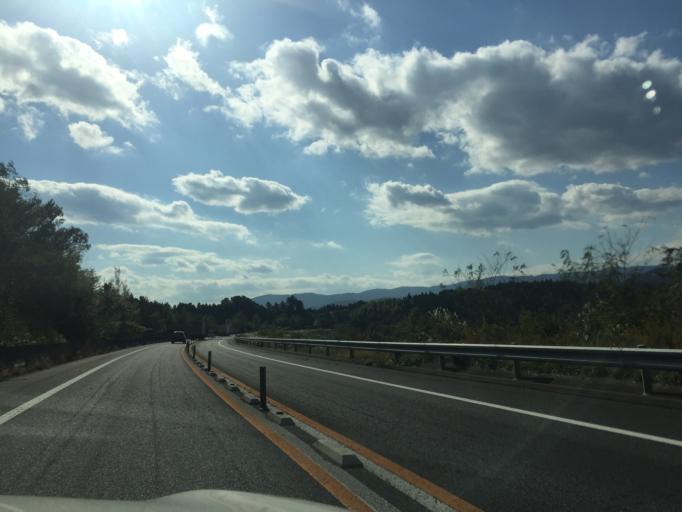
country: JP
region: Fukushima
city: Iwaki
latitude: 37.1007
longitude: 140.8731
